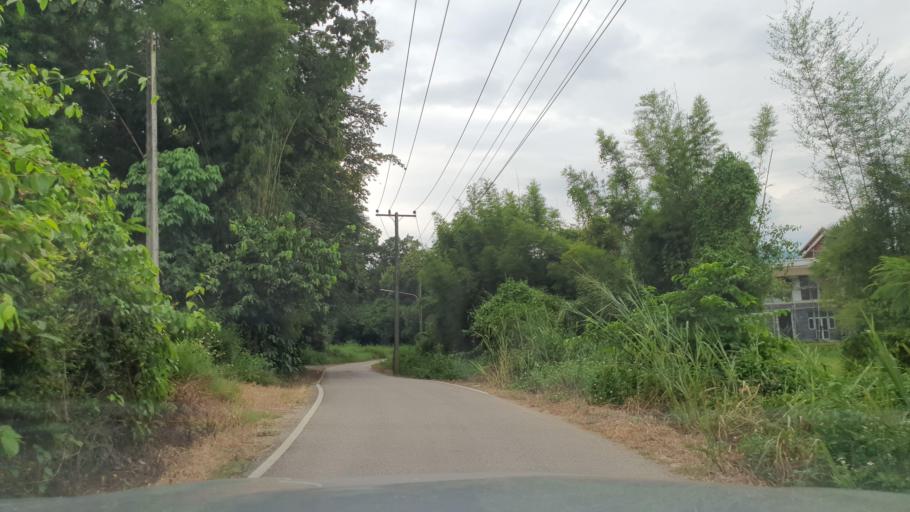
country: TH
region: Chiang Mai
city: San Sai
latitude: 18.9277
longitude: 98.9197
